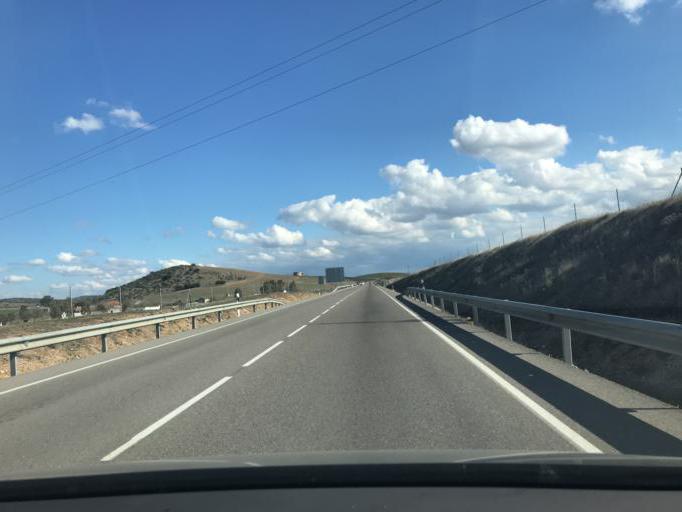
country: ES
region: Andalusia
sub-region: Province of Cordoba
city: Penarroya-Pueblonuevo
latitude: 38.3090
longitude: -5.2654
